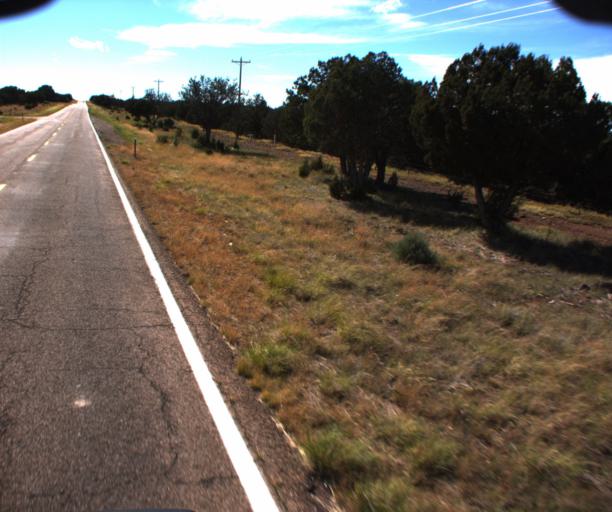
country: US
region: Arizona
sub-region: Navajo County
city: White Mountain Lake
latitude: 34.2991
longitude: -109.7928
